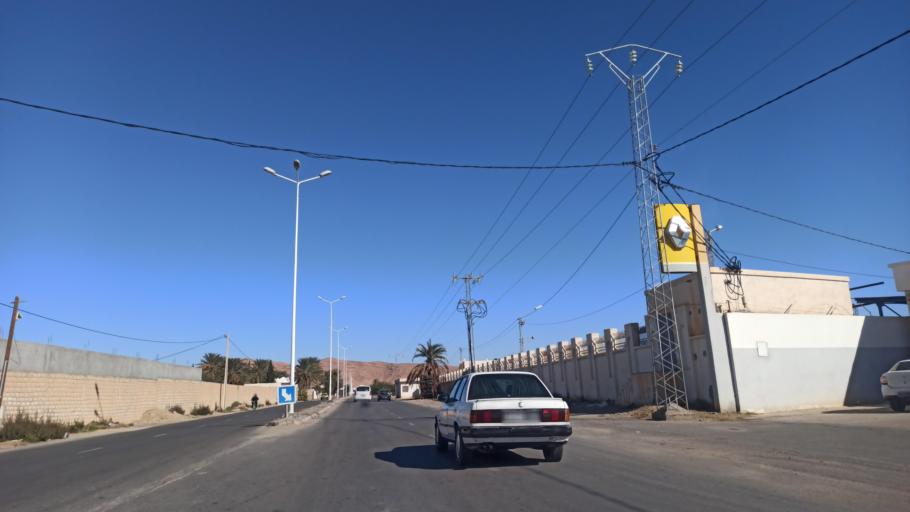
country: TN
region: Gafsa
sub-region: Gafsa Municipality
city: Gafsa
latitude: 34.4110
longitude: 8.7376
